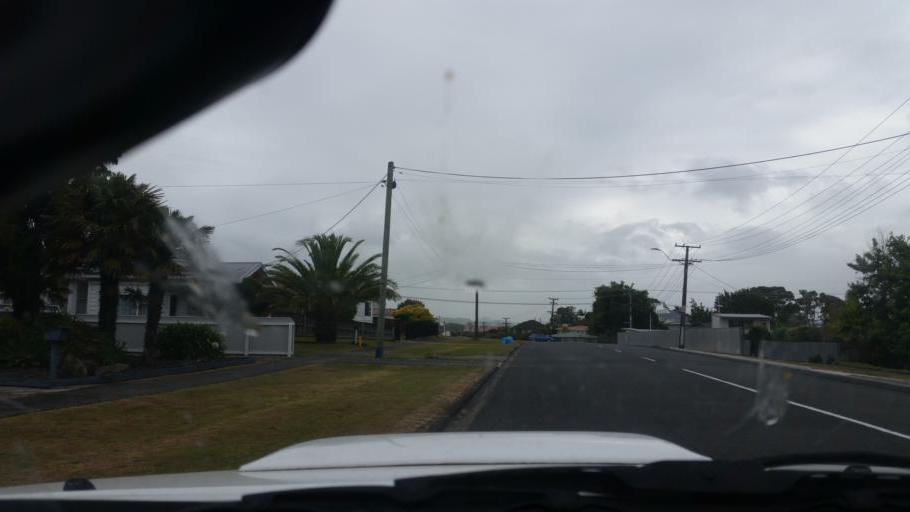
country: NZ
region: Northland
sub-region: Kaipara District
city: Dargaville
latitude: -35.9374
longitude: 173.8677
